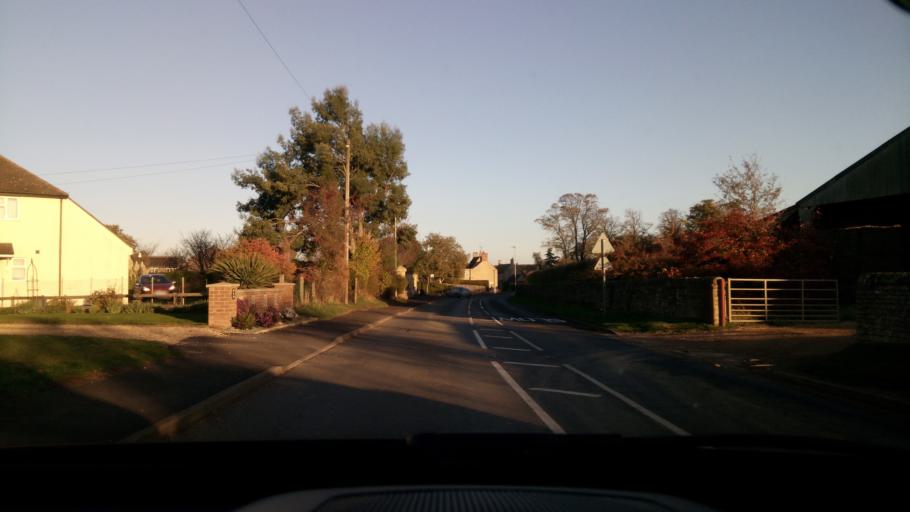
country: GB
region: England
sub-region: Peterborough
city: Barnack
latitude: 52.6344
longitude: -0.4077
